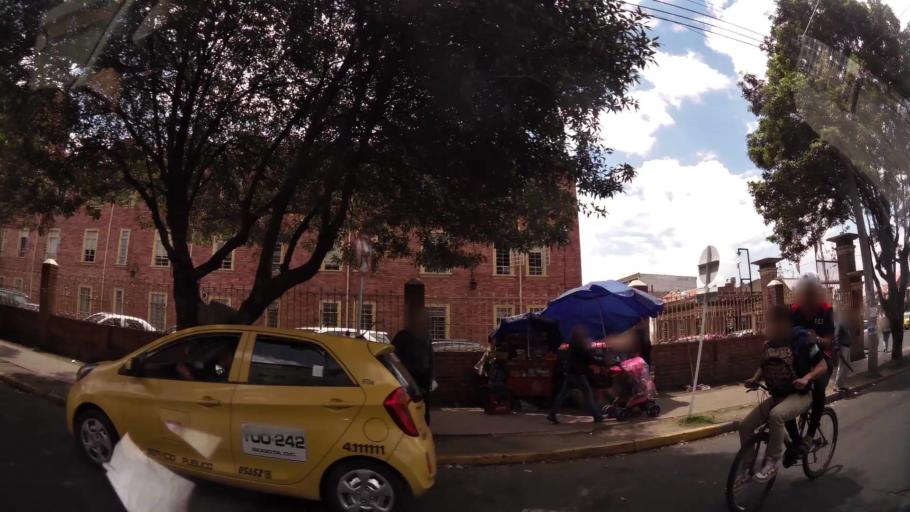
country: CO
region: Bogota D.C.
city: Bogota
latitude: 4.6365
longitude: -74.0734
